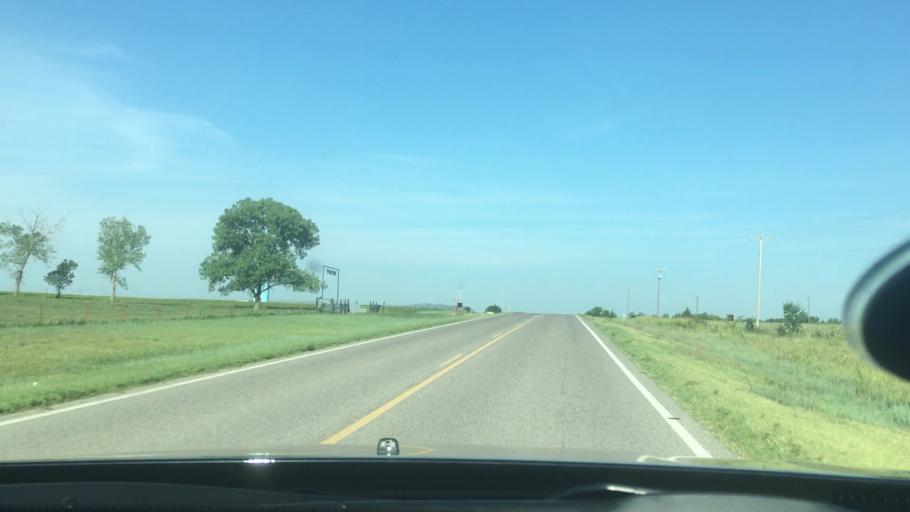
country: US
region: Oklahoma
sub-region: Garvin County
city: Pauls Valley
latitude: 34.6518
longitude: -97.2797
